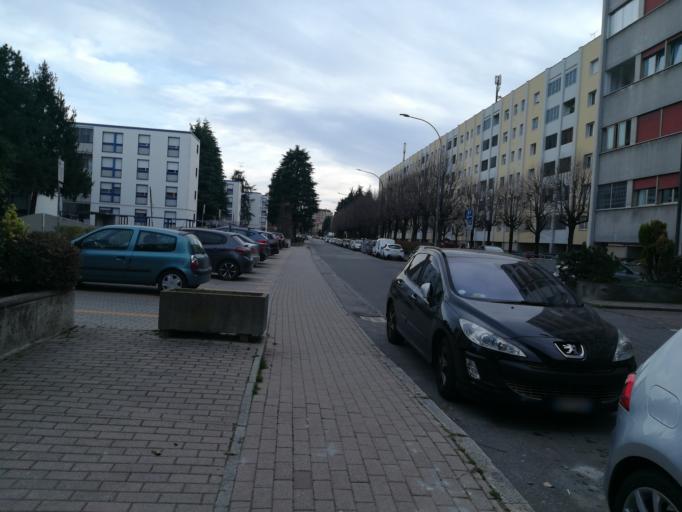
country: IT
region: Emilia-Romagna
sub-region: Provincia di Bologna
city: Progresso
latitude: 44.5449
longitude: 11.3601
